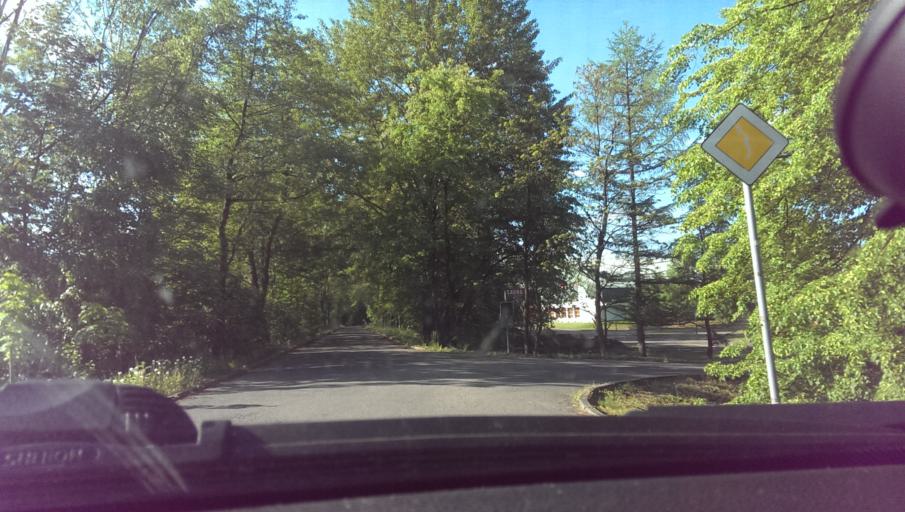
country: CZ
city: Frydlant nad Ostravici
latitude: 49.5819
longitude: 18.3652
